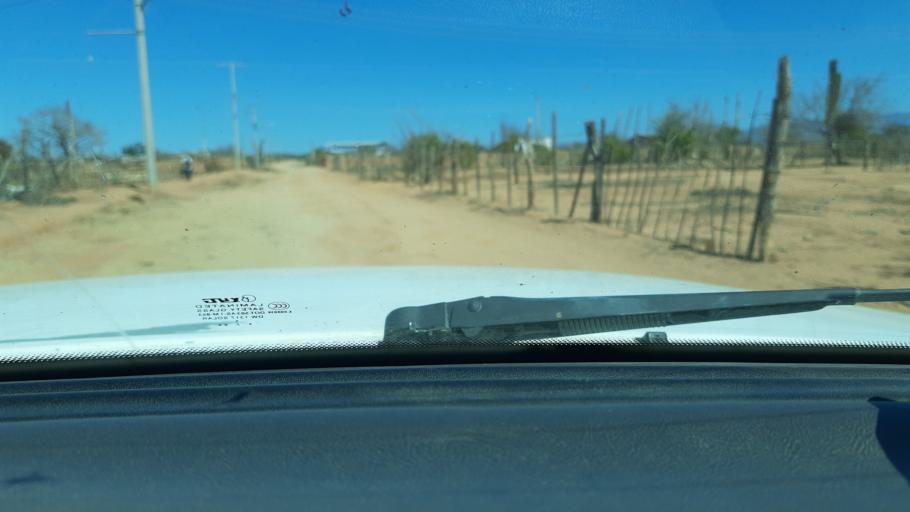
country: MX
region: Baja California Sur
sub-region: La Paz
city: Meliton Albanez Dominguez
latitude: 23.6463
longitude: -110.2626
